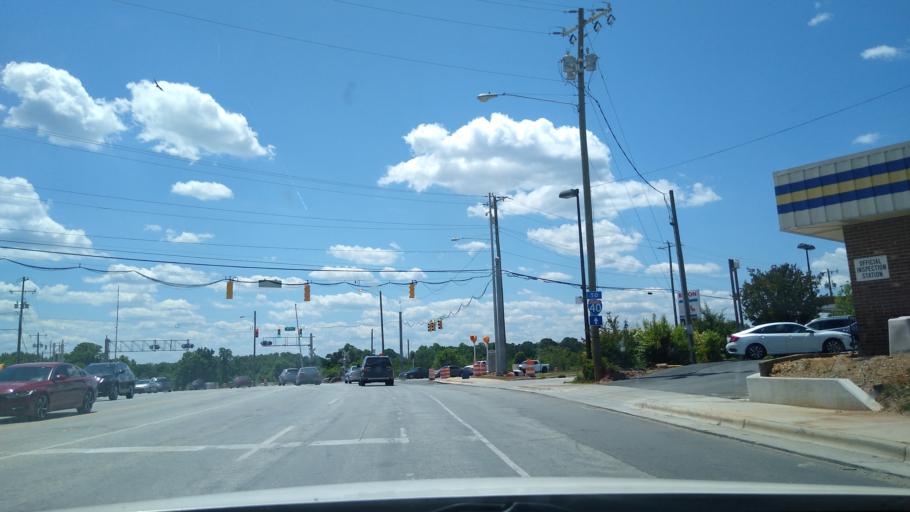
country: US
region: North Carolina
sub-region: Guilford County
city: Jamestown
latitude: 36.0773
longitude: -79.8972
